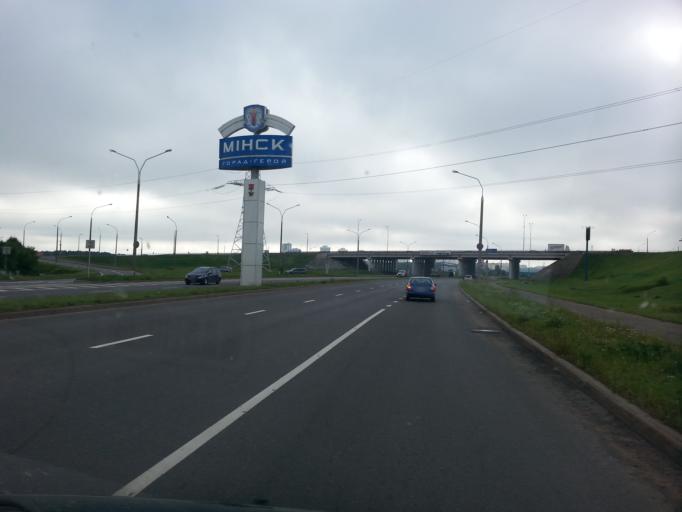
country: BY
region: Minsk
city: Zhdanovichy
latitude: 53.9449
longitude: 27.4333
